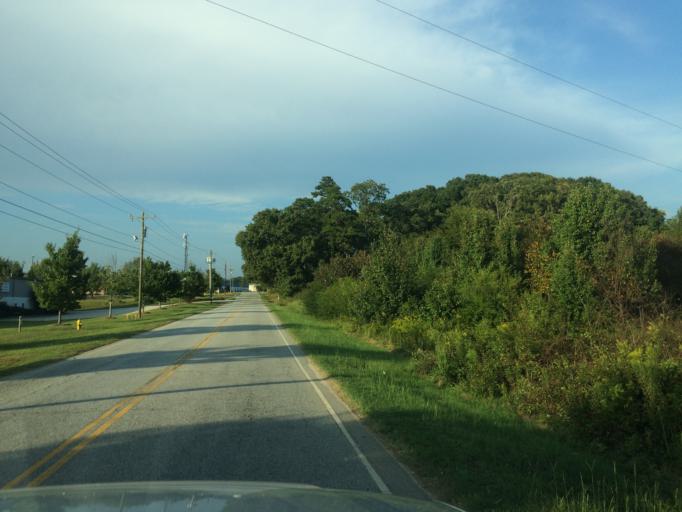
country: US
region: South Carolina
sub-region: Anderson County
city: Piedmont
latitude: 34.6992
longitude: -82.5049
